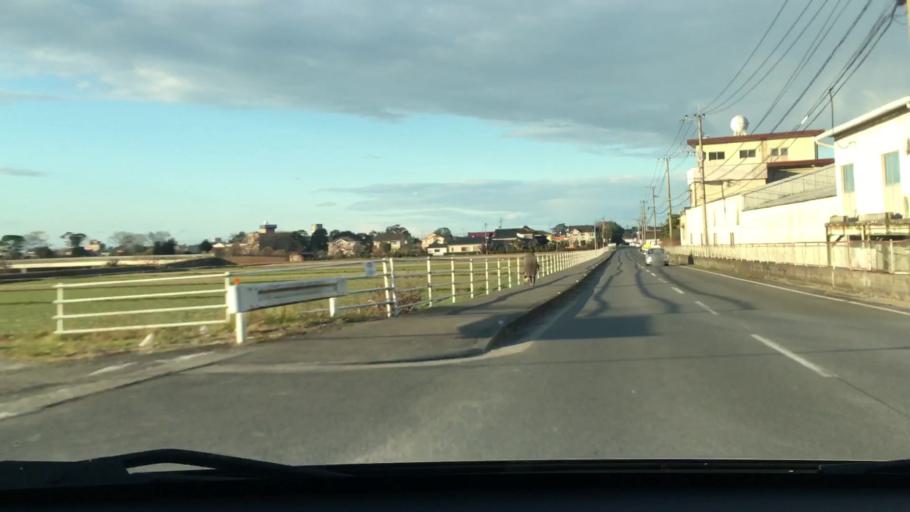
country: JP
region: Oita
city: Bungo-Takada-shi
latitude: 33.5184
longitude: 131.3483
